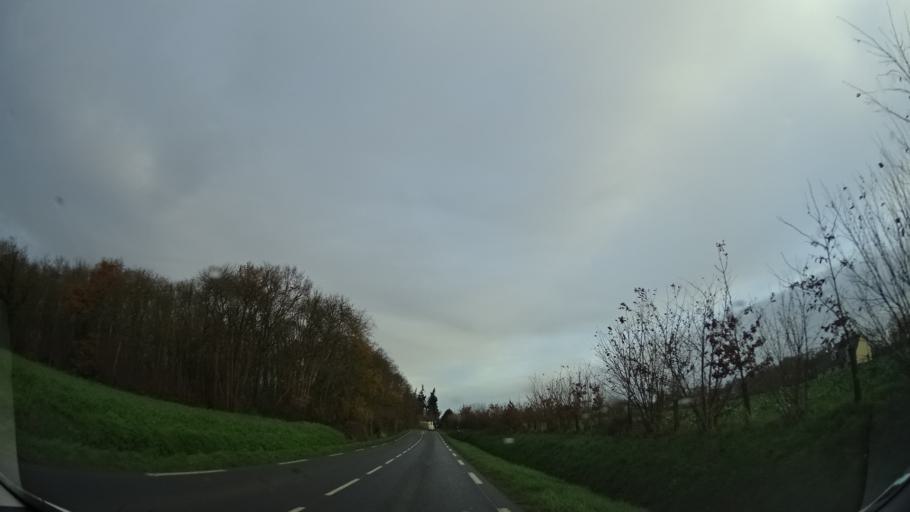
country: FR
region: Brittany
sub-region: Departement des Cotes-d'Armor
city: Evran
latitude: 48.3931
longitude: -1.9799
